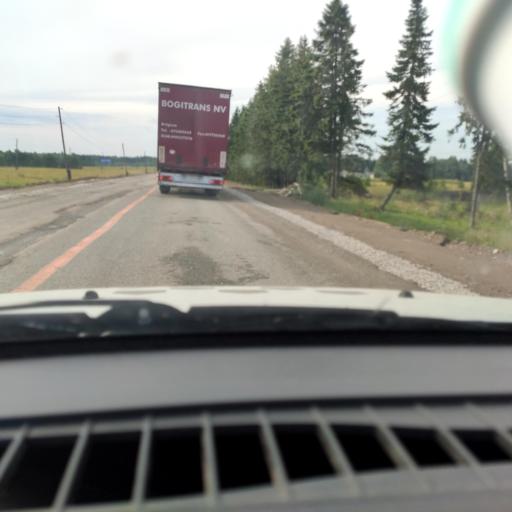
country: RU
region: Kirov
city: Kostino
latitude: 58.8283
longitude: 53.3087
